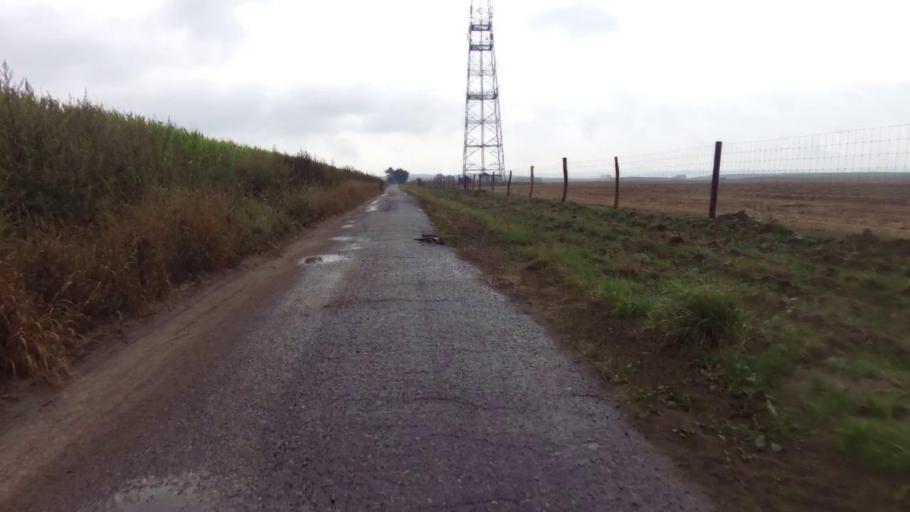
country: PL
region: West Pomeranian Voivodeship
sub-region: Powiat choszczenski
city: Recz
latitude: 53.2663
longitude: 15.4609
